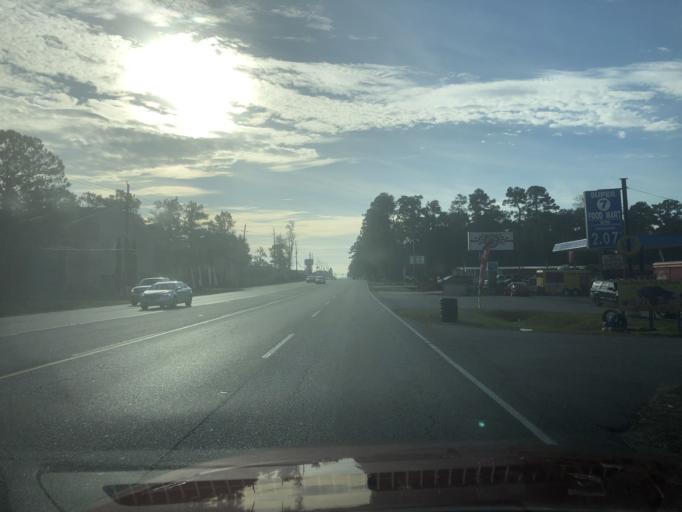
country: US
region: Texas
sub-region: Harris County
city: Spring
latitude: 30.0185
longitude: -95.4721
